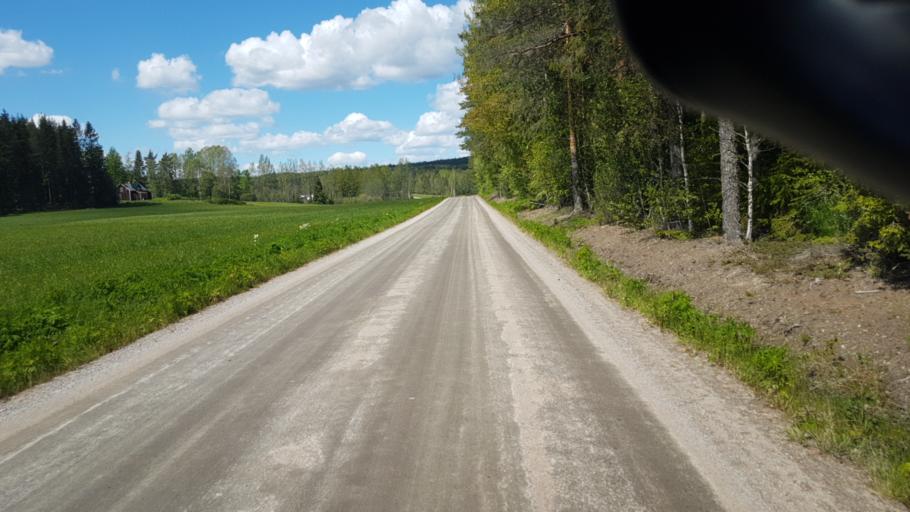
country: SE
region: Vaermland
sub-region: Arvika Kommun
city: Arvika
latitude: 59.6153
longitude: 12.9011
